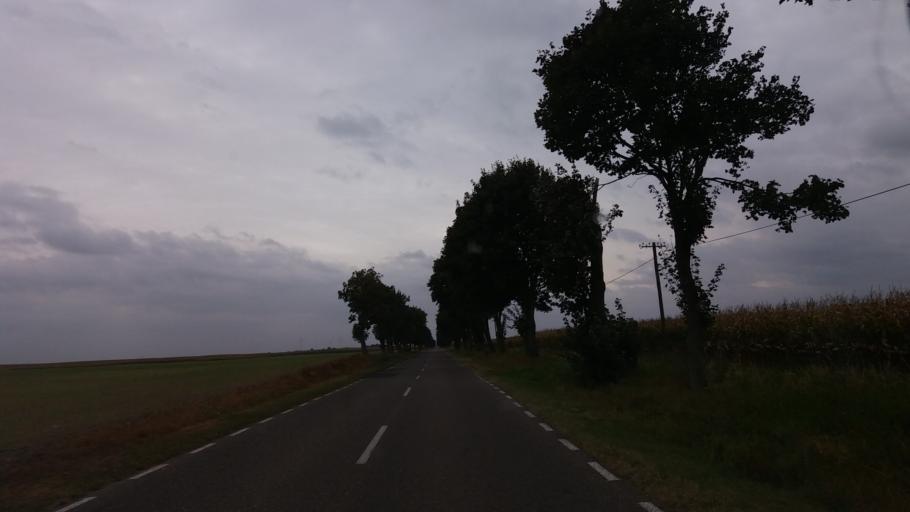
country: PL
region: Lubusz
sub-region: Powiat strzelecko-drezdenecki
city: Strzelce Krajenskie
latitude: 52.9549
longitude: 15.5730
